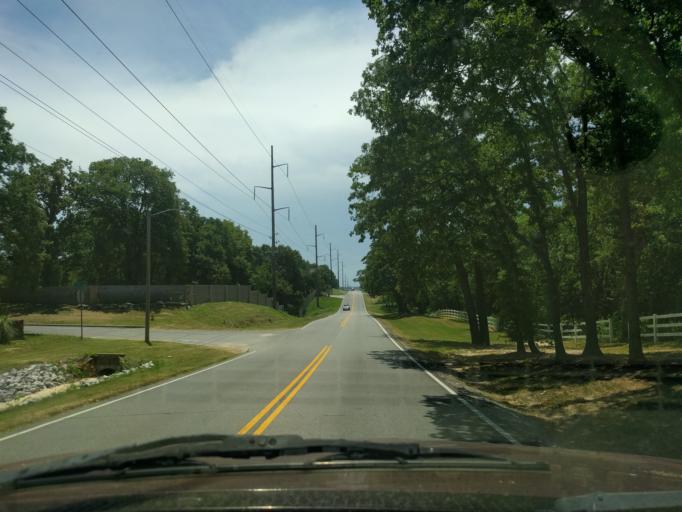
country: US
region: Oklahoma
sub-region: Tulsa County
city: Jenks
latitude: 36.0005
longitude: -95.9223
